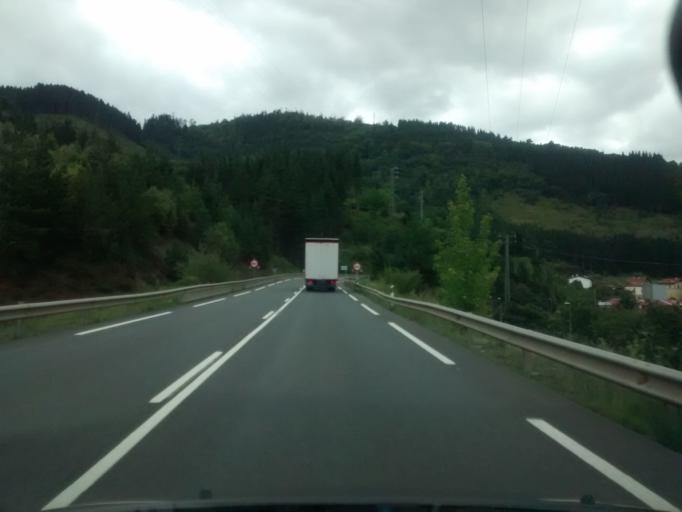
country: ES
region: Basque Country
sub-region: Provincia de Guipuzcoa
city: Arrasate / Mondragon
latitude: 43.0646
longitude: -2.4776
